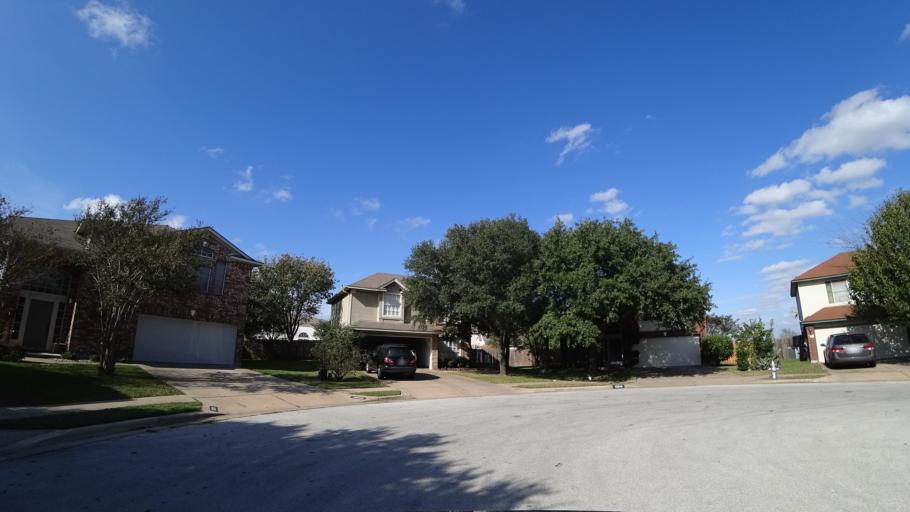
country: US
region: Texas
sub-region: Travis County
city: Wells Branch
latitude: 30.4593
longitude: -97.6804
